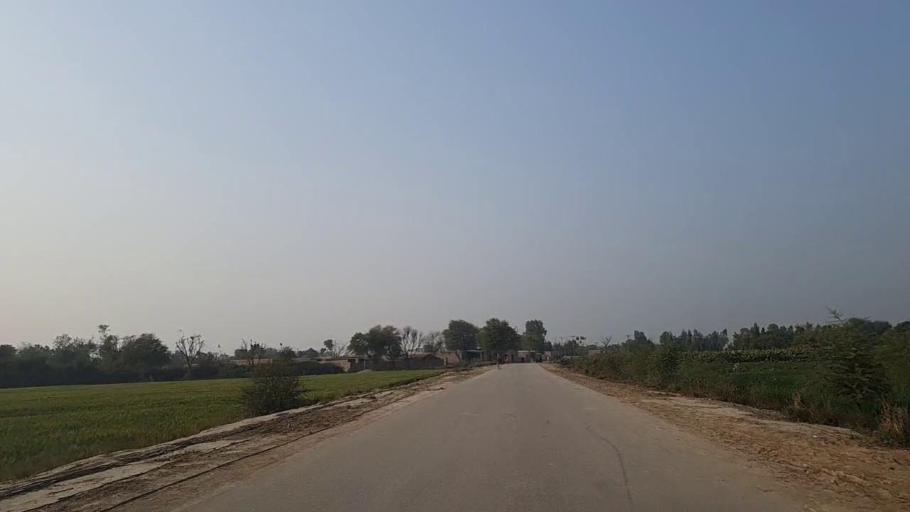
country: PK
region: Sindh
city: Sann
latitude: 26.1222
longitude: 68.1475
